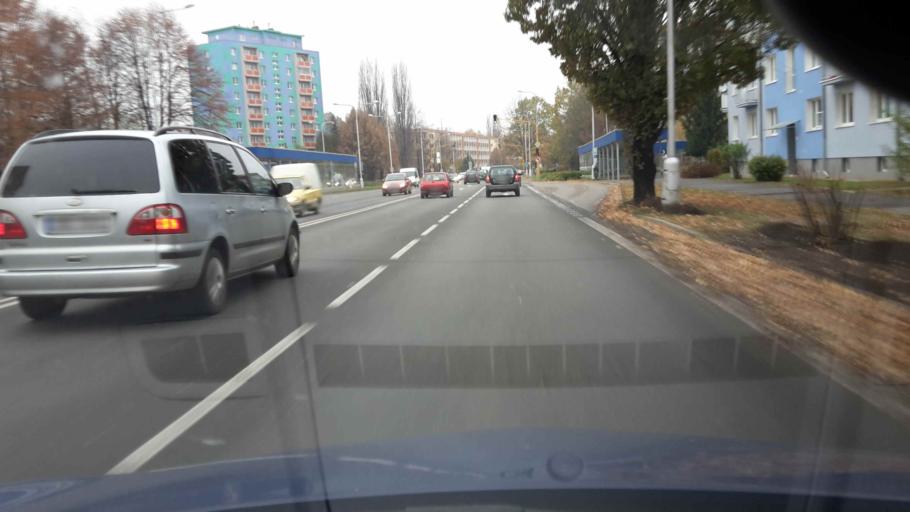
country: CZ
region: Olomoucky
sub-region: Okres Olomouc
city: Olomouc
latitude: 49.5911
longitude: 17.2361
